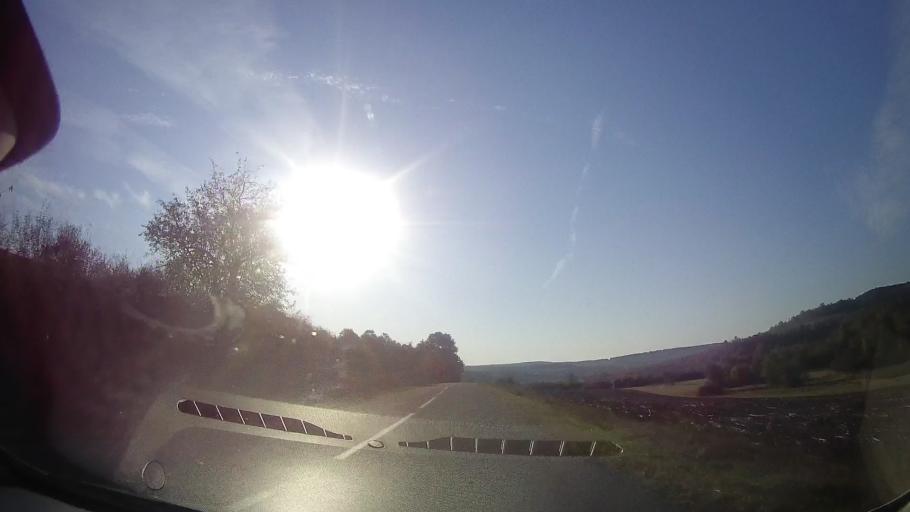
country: RO
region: Timis
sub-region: Comuna Bogda
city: Bogda
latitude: 45.9708
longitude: 21.6031
